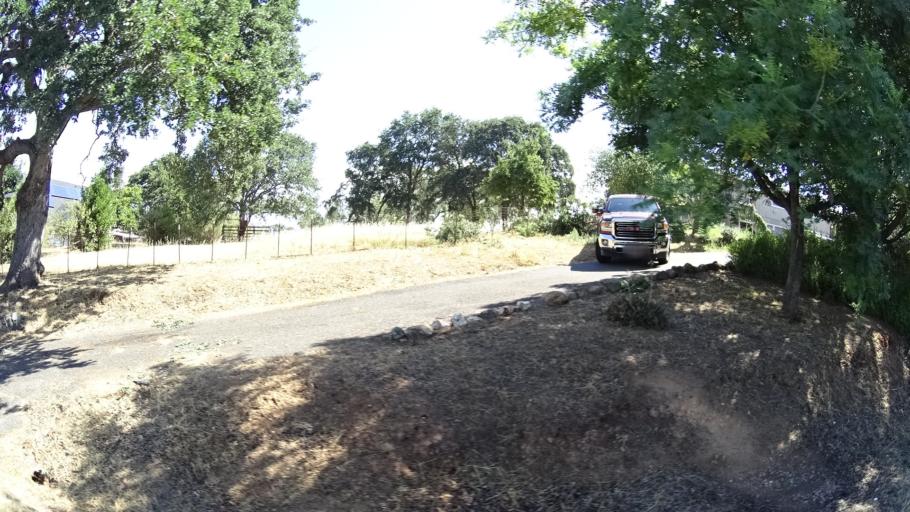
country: US
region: California
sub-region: Calaveras County
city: Copperopolis
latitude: 37.9296
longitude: -120.6334
